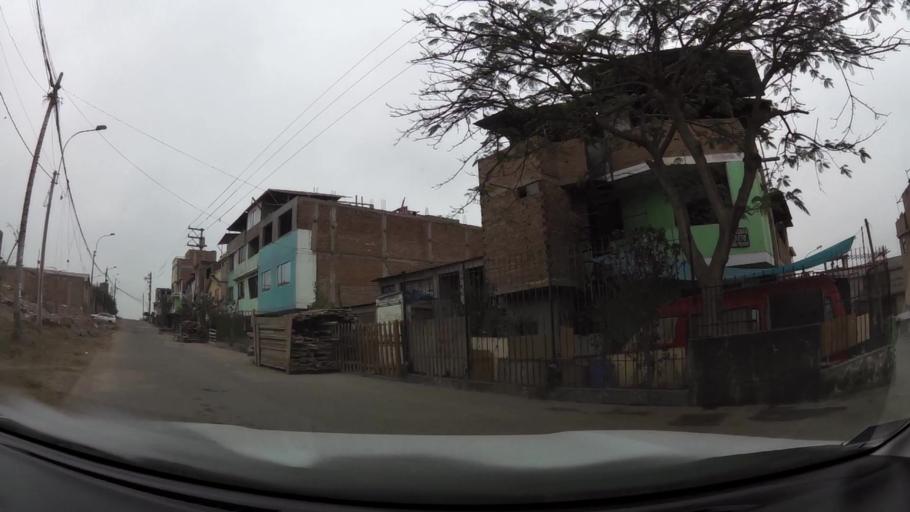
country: PE
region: Lima
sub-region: Lima
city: Surco
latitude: -12.1664
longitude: -76.9593
